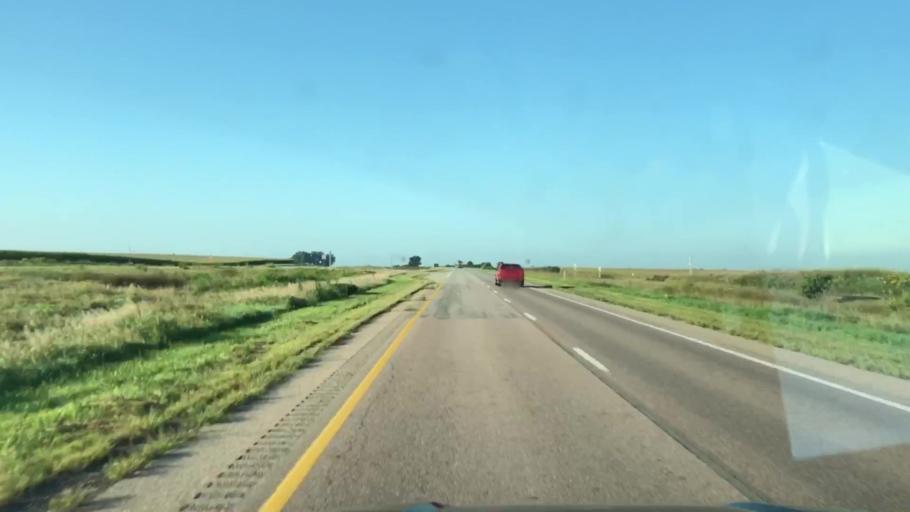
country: US
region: Iowa
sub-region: O'Brien County
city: Sheldon
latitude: 43.1143
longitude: -95.8951
